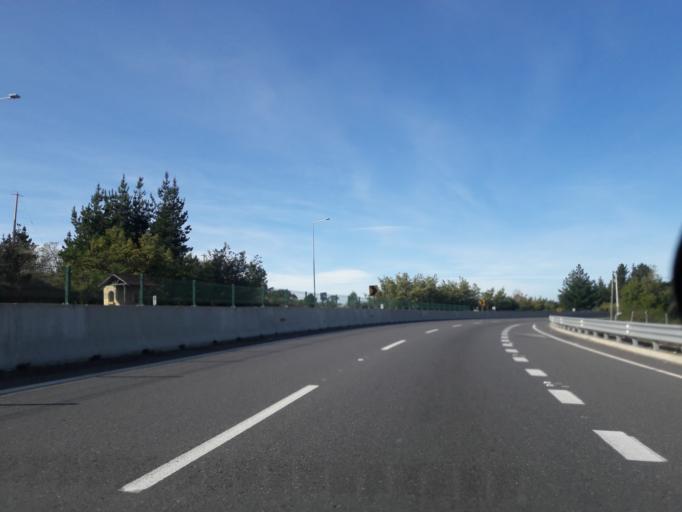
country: CL
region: Biobio
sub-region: Provincia de Biobio
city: Yumbel
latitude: -36.9740
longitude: -72.6543
